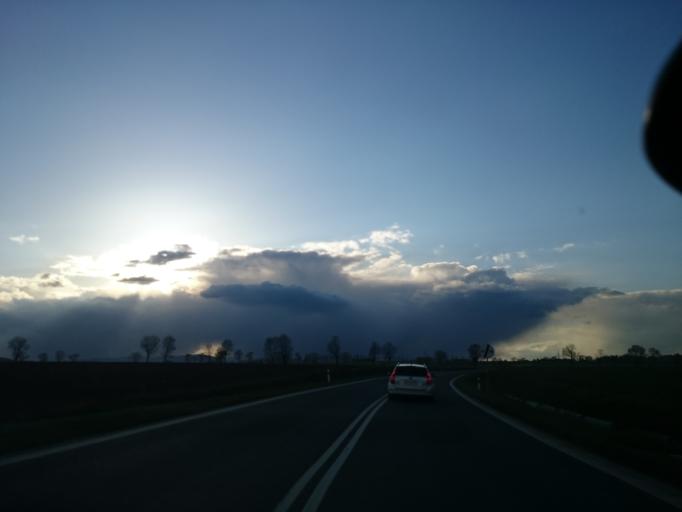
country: PL
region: Lower Silesian Voivodeship
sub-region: Powiat zabkowicki
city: Zabkowice Slaskie
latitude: 50.5713
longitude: 16.8263
